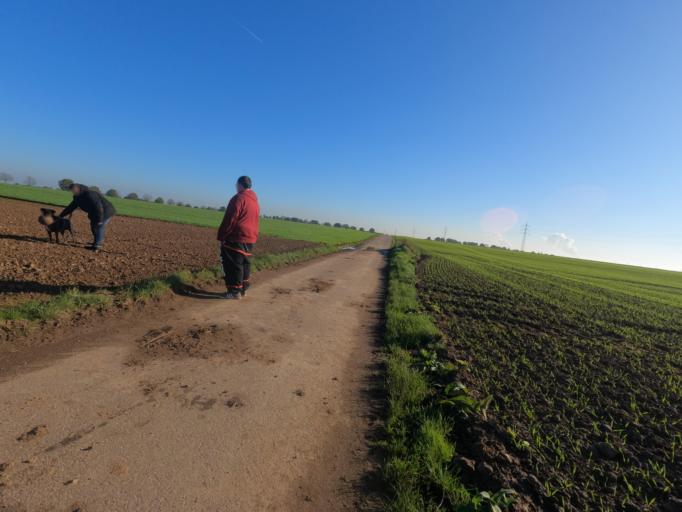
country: DE
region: North Rhine-Westphalia
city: Erkelenz
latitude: 51.0856
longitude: 6.3527
